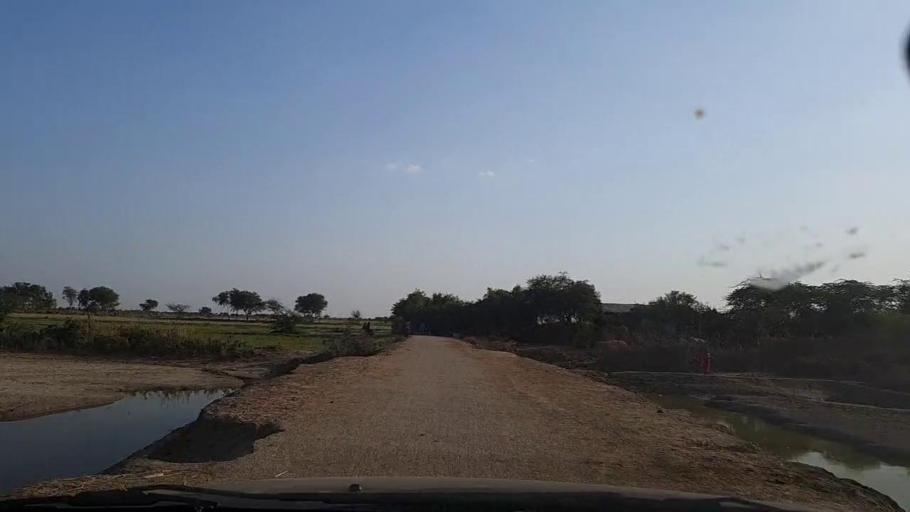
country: PK
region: Sindh
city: Daro Mehar
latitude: 24.7465
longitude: 68.0944
